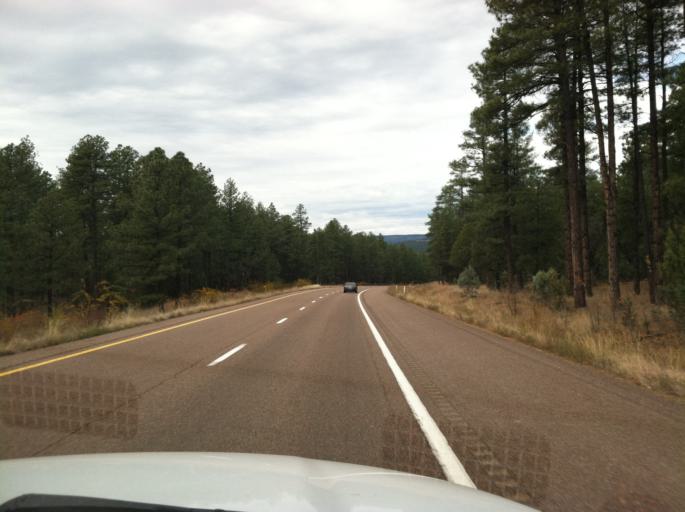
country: US
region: Arizona
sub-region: Gila County
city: Star Valley
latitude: 34.2957
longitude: -110.9811
